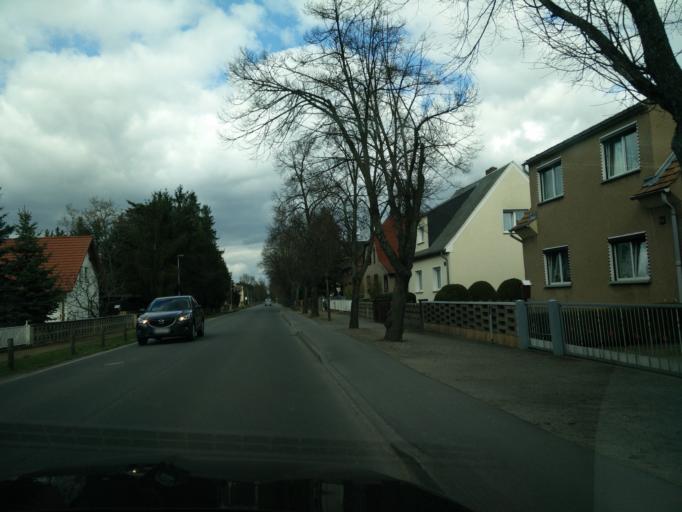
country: DE
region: Brandenburg
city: Bad Liebenwerda
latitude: 51.5265
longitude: 13.3977
